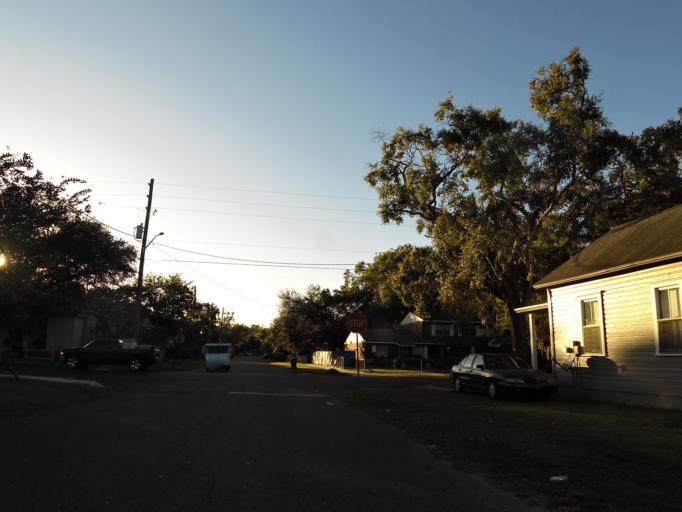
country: US
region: Florida
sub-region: Duval County
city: Jacksonville
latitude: 30.3398
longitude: -81.6465
